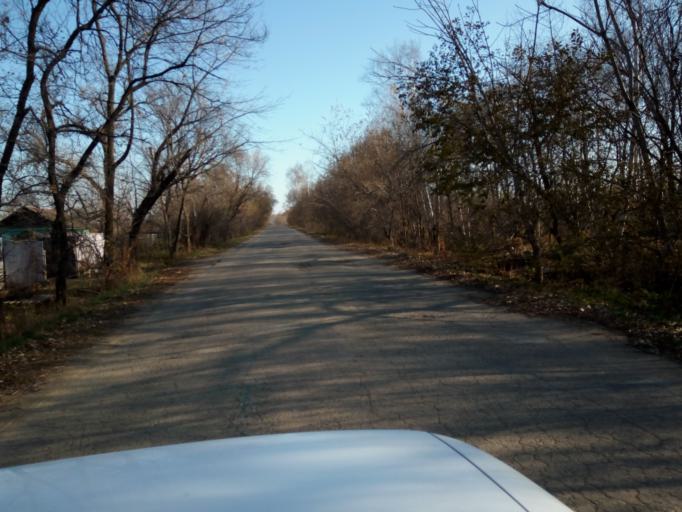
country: RU
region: Primorskiy
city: Lazo
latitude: 45.8822
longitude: 133.6486
